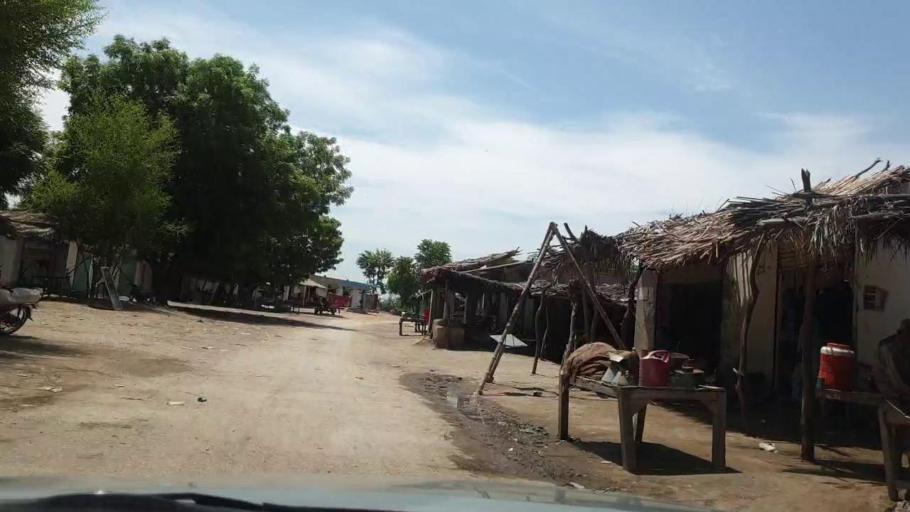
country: PK
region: Sindh
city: Bozdar
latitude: 27.0331
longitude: 68.9574
